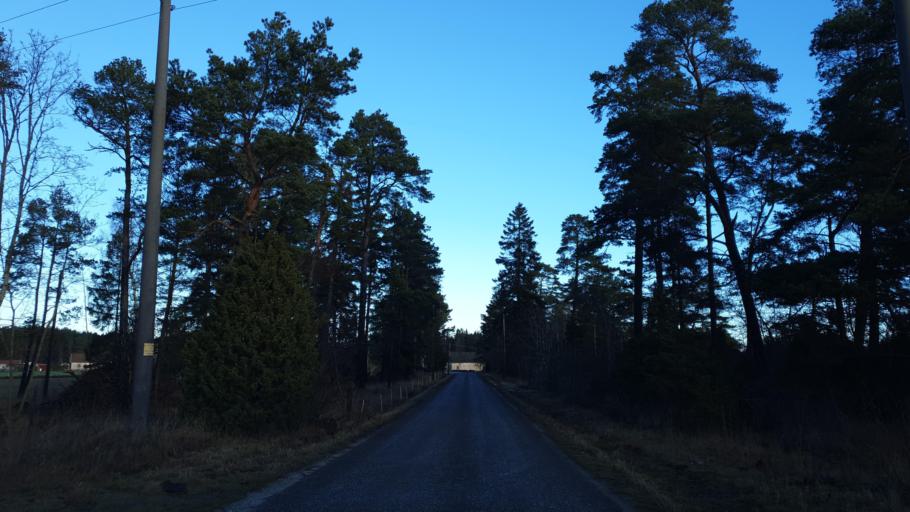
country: SE
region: Gotland
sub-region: Gotland
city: Slite
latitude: 57.3822
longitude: 18.8073
